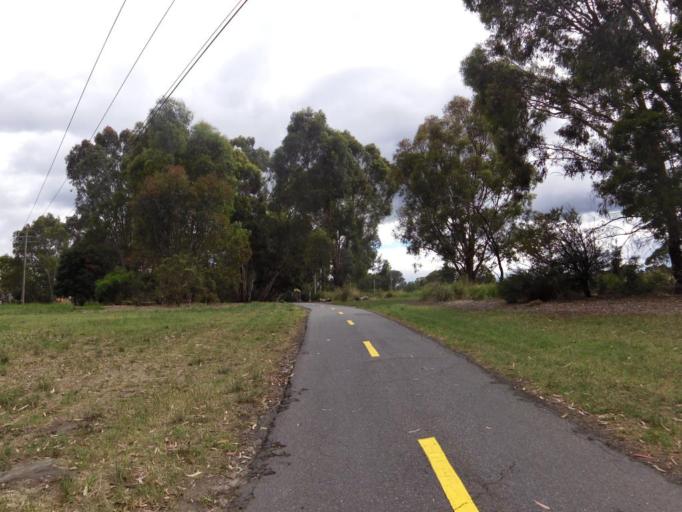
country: AU
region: Victoria
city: Heidelberg West
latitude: -37.7385
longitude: 145.0327
